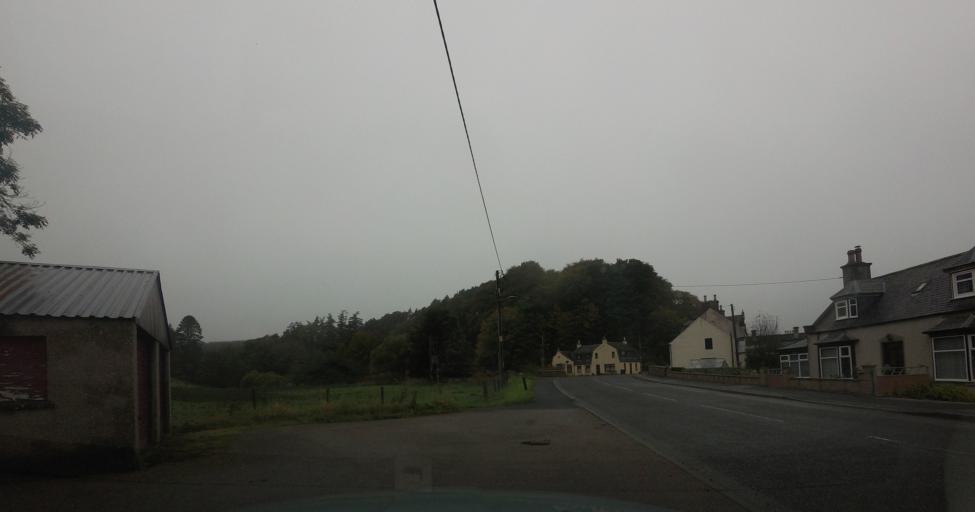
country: GB
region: Scotland
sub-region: Aberdeenshire
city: Oldmeldrum
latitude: 57.4278
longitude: -2.3975
